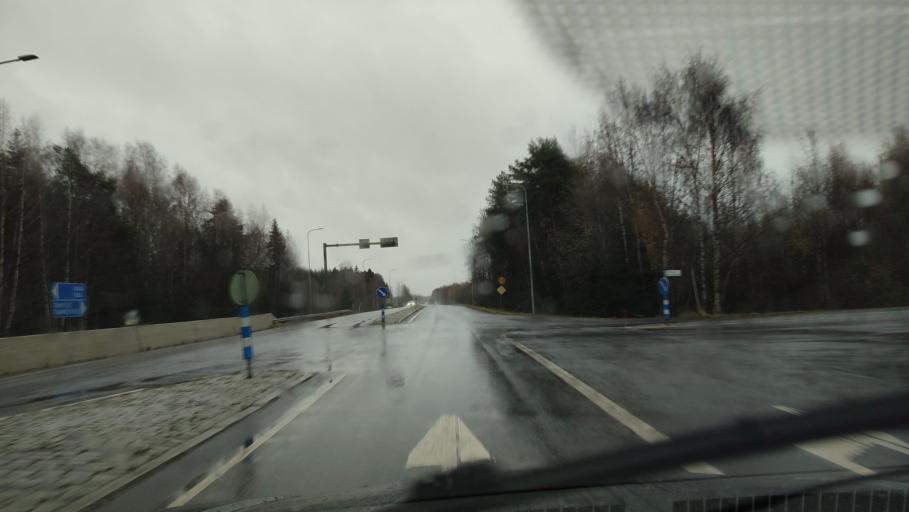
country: FI
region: Ostrobothnia
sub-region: Vaasa
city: Ristinummi
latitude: 63.0529
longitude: 21.7218
